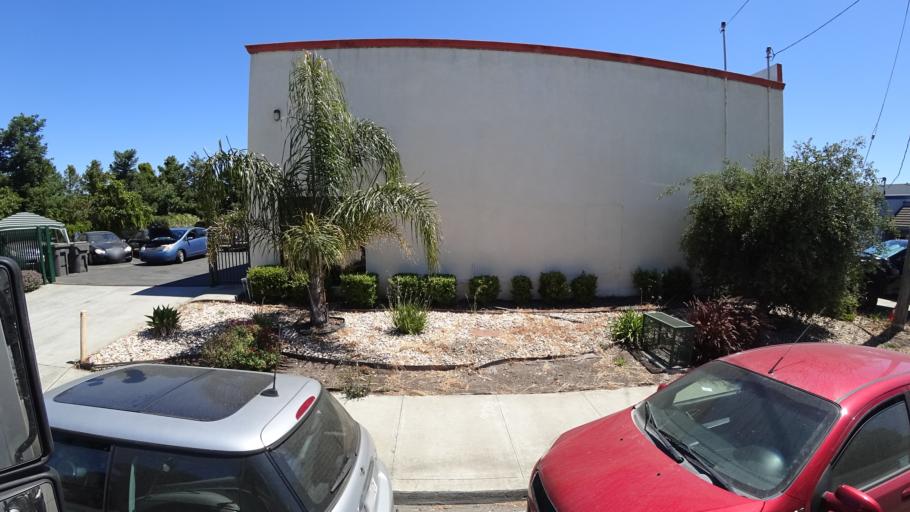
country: US
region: California
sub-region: Alameda County
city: Hayward
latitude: 37.6200
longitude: -122.0984
